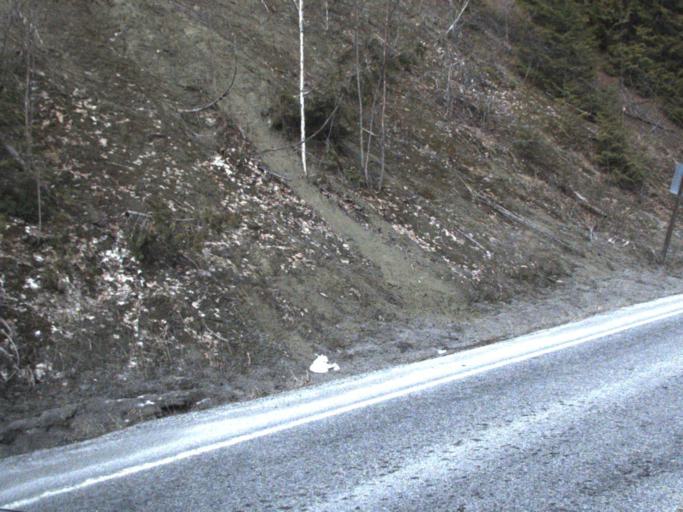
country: US
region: Washington
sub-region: Stevens County
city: Chewelah
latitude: 48.5665
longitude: -117.3544
